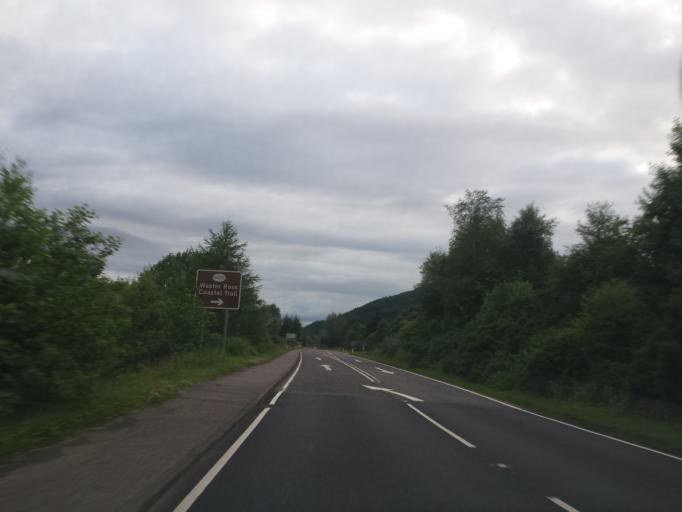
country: GB
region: Scotland
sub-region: Highland
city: Portree
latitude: 57.2855
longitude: -5.5780
